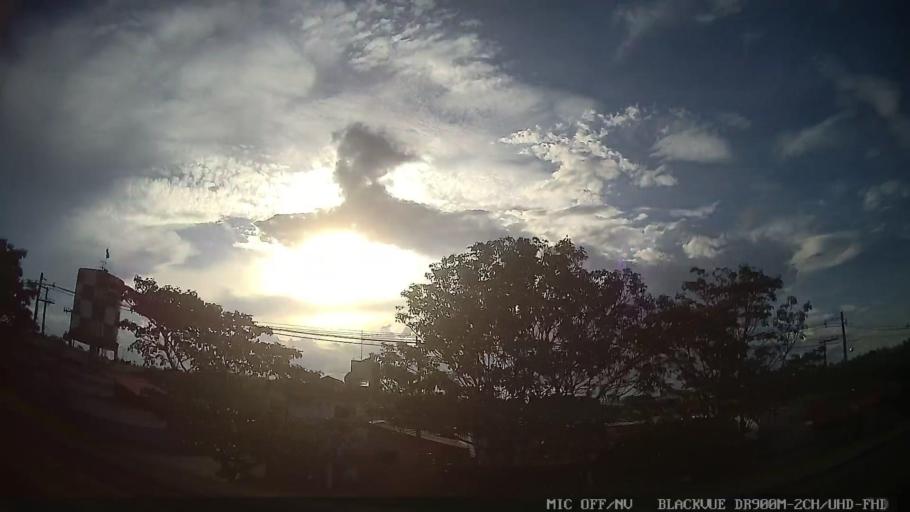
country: BR
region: Sao Paulo
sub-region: Tiete
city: Tiete
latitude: -23.1041
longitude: -47.7247
